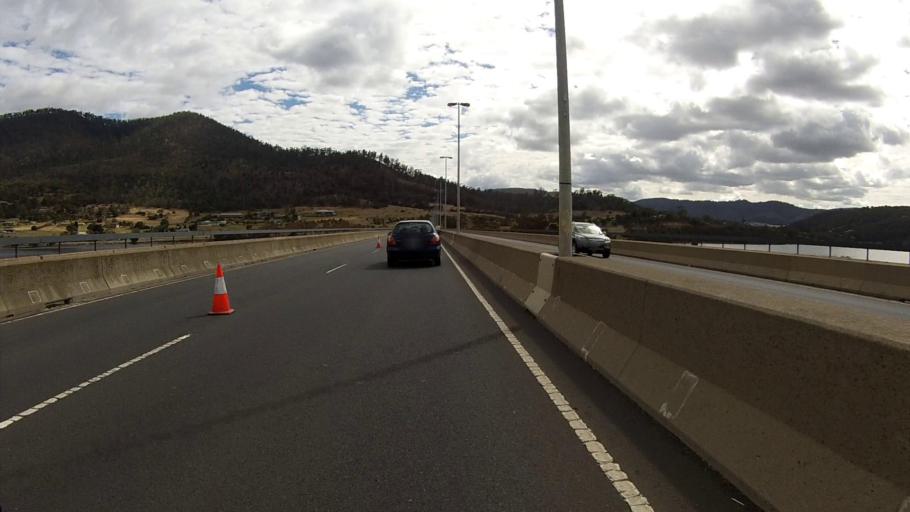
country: AU
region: Tasmania
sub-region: Glenorchy
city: Goodwood
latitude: -42.8180
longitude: 147.3066
